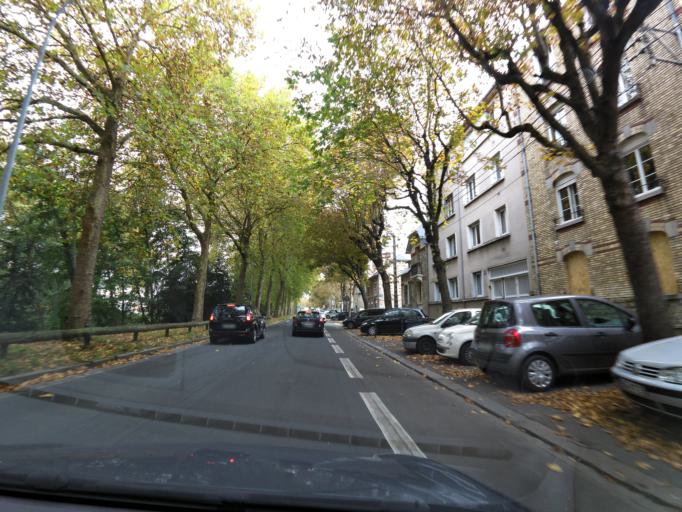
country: FR
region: Brittany
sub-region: Departement d'Ille-et-Vilaine
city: Rennes
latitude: 48.1160
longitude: -1.6867
